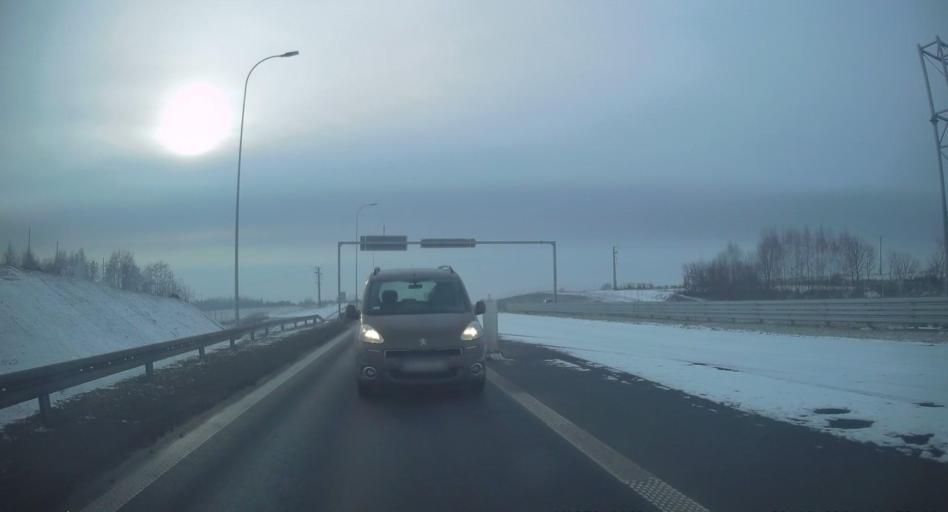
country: PL
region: Lesser Poland Voivodeship
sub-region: Powiat miechowski
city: Miechow
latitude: 50.3107
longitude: 20.0343
